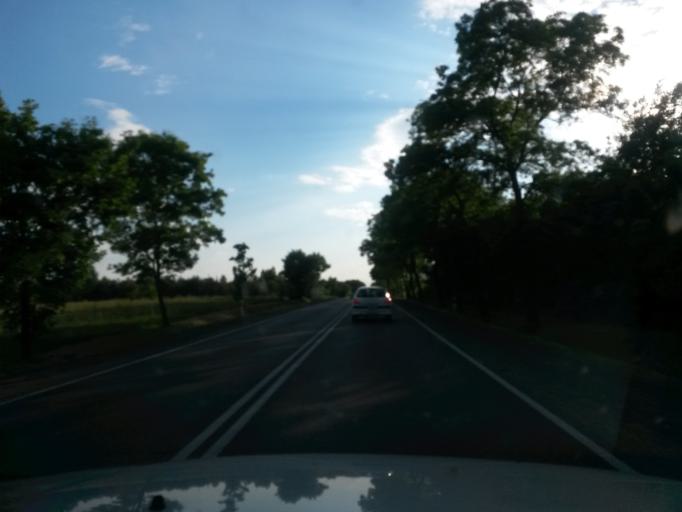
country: PL
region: Lodz Voivodeship
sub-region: Powiat belchatowski
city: Kluki
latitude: 51.3422
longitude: 19.2200
